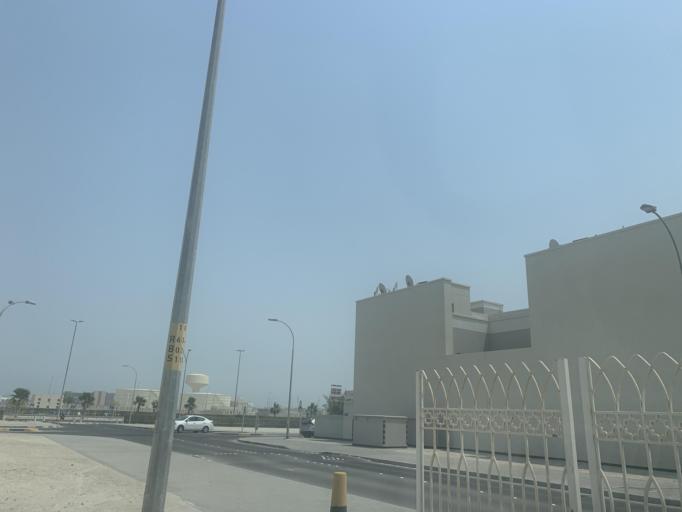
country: BH
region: Muharraq
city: Al Muharraq
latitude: 26.3089
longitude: 50.6289
